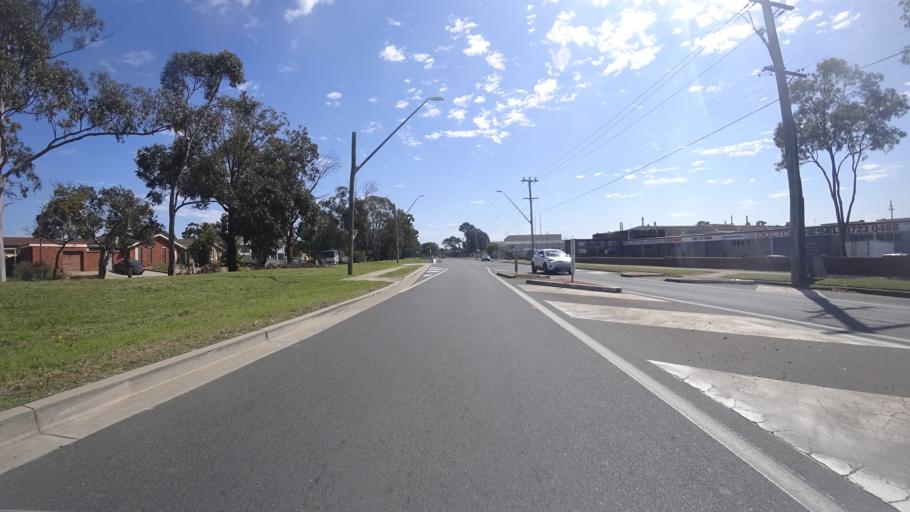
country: AU
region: New South Wales
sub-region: Fairfield
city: Chipping Norton
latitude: -33.9188
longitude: 150.9617
